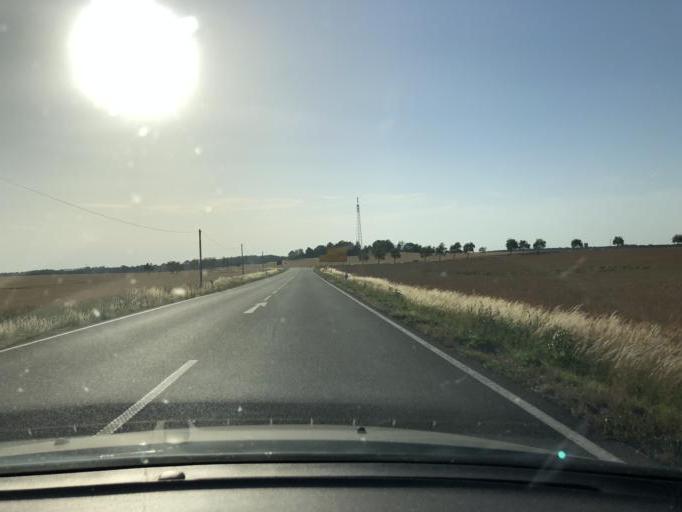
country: DE
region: Saxony
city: Falkenhain
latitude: 51.3402
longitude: 12.8684
